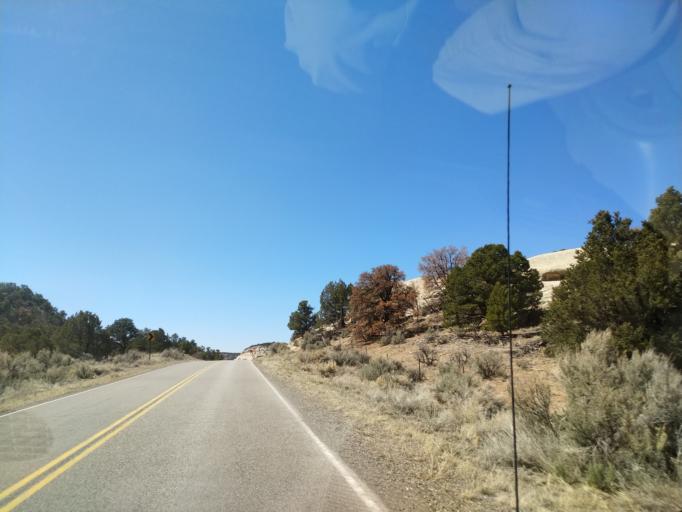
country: US
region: Colorado
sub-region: Mesa County
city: Redlands
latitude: 38.9866
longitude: -108.7887
